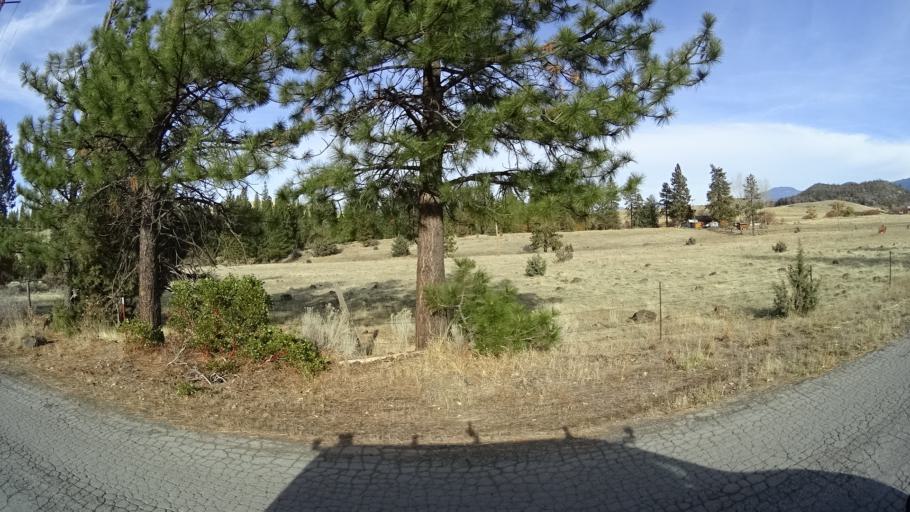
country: US
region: California
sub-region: Siskiyou County
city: Weed
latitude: 41.4656
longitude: -122.4036
